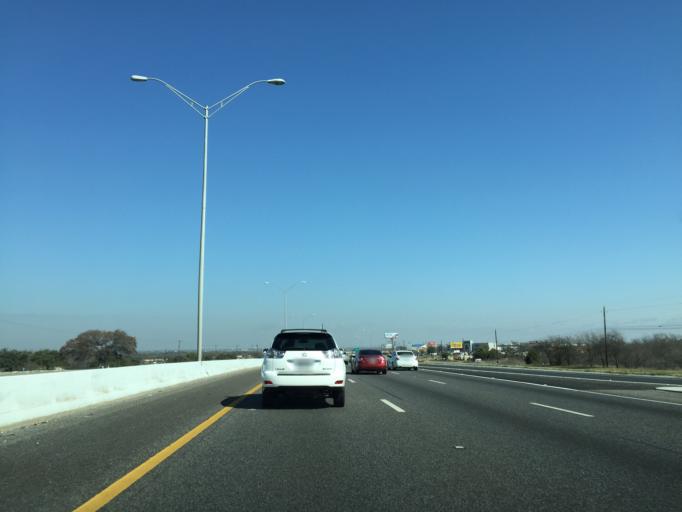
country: US
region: Texas
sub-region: Williamson County
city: Georgetown
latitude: 30.5884
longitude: -97.6923
